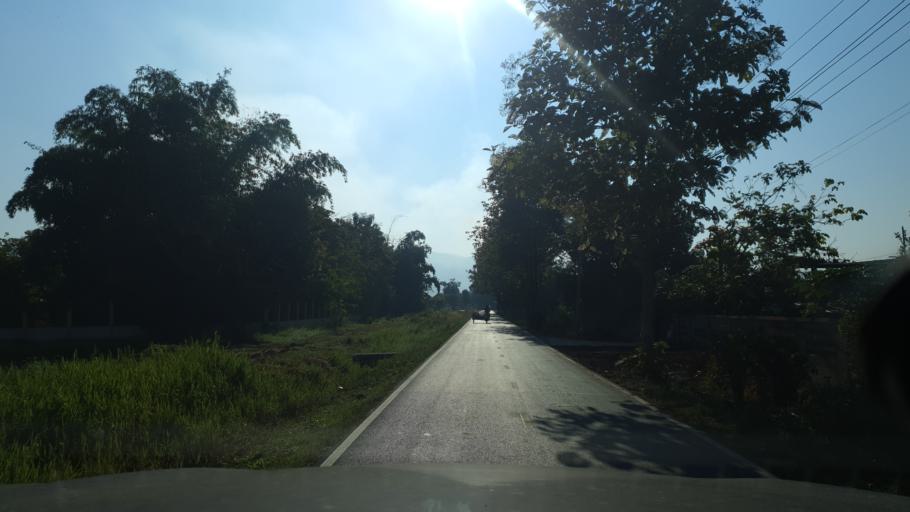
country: TH
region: Chiang Mai
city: San Kamphaeng
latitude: 18.6933
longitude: 99.1533
